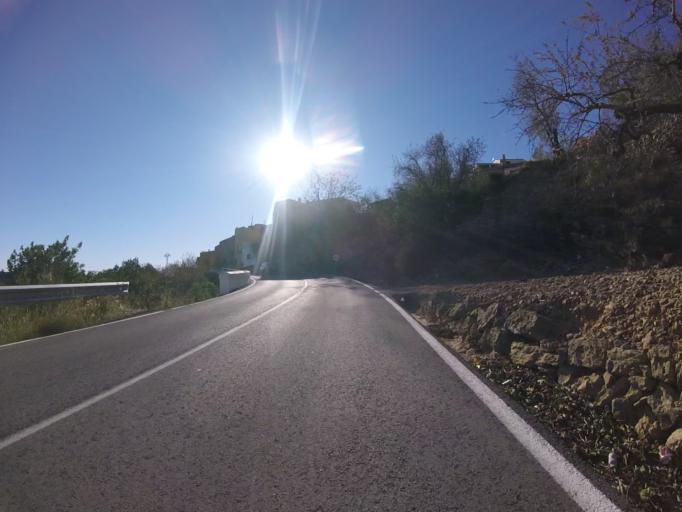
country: ES
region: Valencia
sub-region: Provincia de Castello
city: Cervera del Maestre
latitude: 40.4551
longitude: 0.2793
